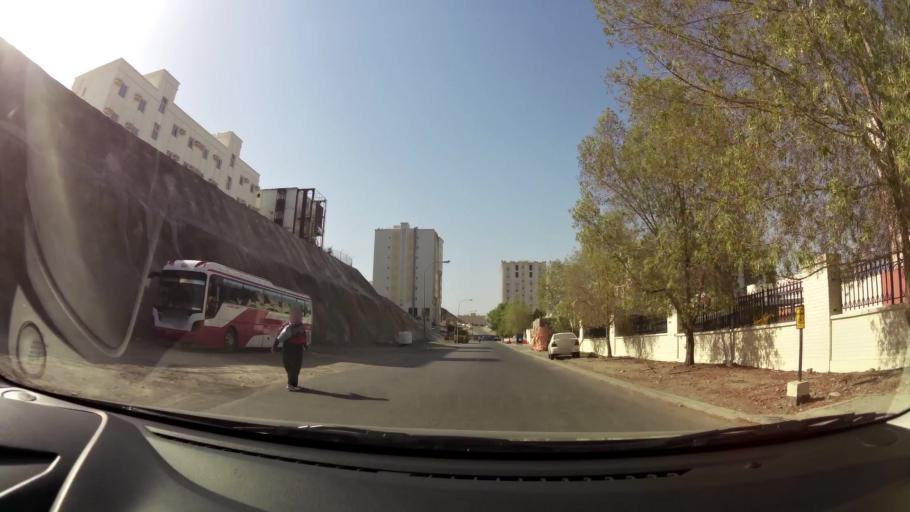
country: OM
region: Muhafazat Masqat
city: Muscat
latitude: 23.5984
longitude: 58.5530
